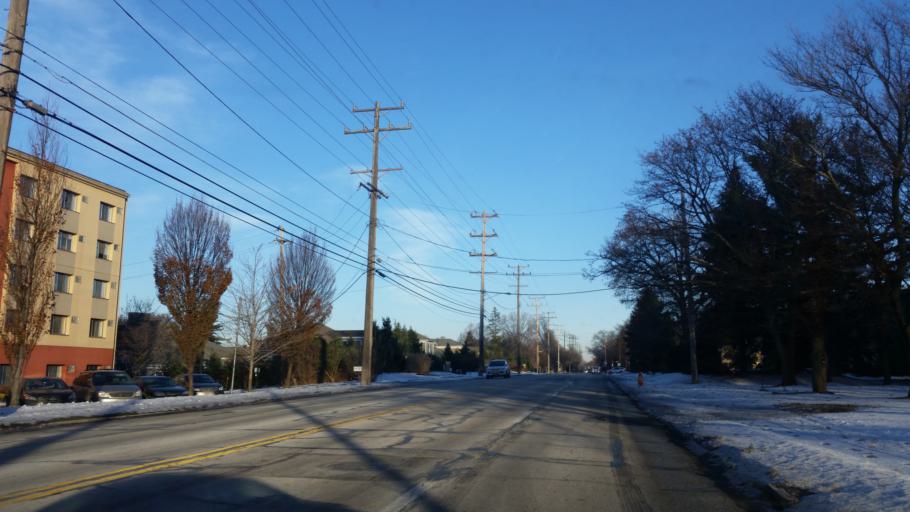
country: US
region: Ohio
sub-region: Cuyahoga County
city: Fairview Park
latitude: 41.4567
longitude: -81.8737
